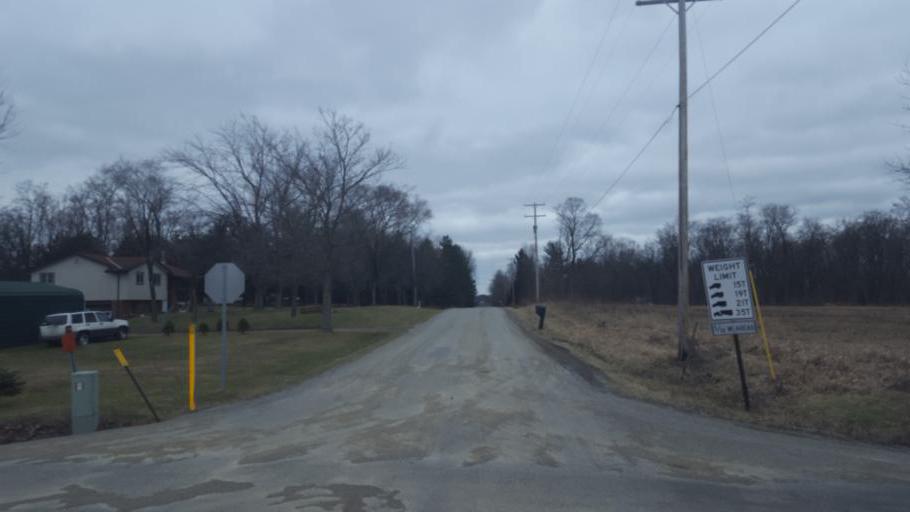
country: US
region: Ohio
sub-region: Crawford County
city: Crestline
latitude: 40.7184
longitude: -82.6891
